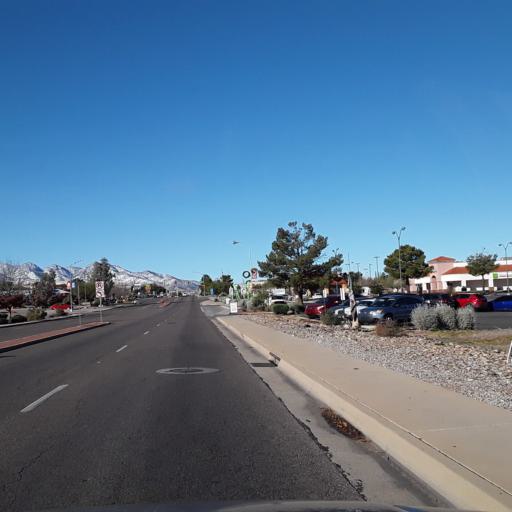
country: US
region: Arizona
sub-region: Cochise County
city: Sierra Vista
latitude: 31.5547
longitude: -110.2745
